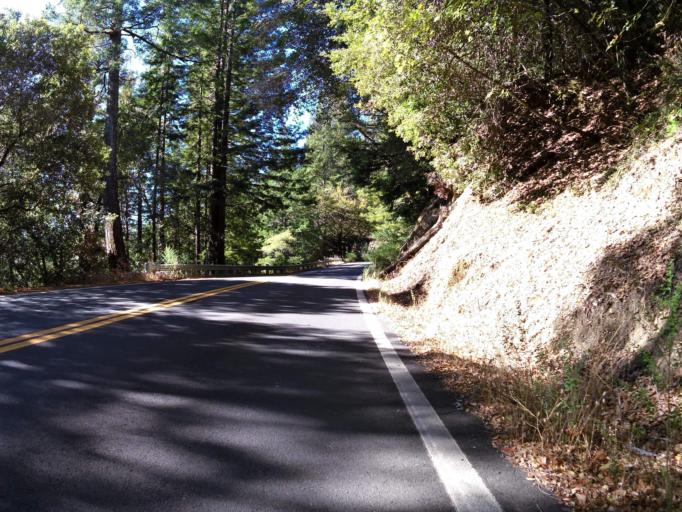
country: US
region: California
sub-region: Humboldt County
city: Redway
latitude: 39.8615
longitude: -123.7260
